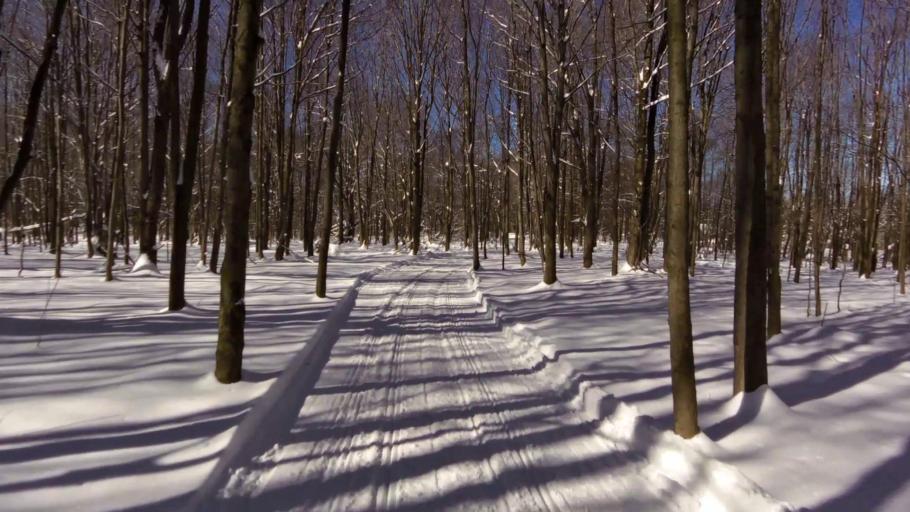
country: US
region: New York
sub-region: Chautauqua County
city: Mayville
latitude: 42.2258
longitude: -79.4034
